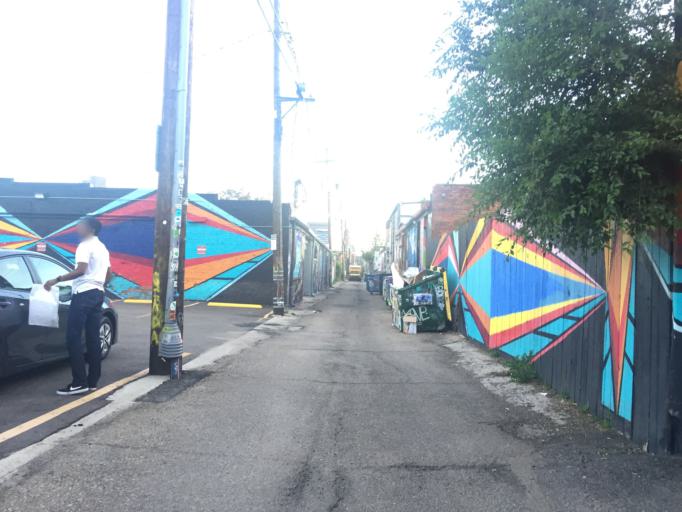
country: US
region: Colorado
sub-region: Denver County
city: Denver
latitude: 39.7606
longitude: -104.9836
